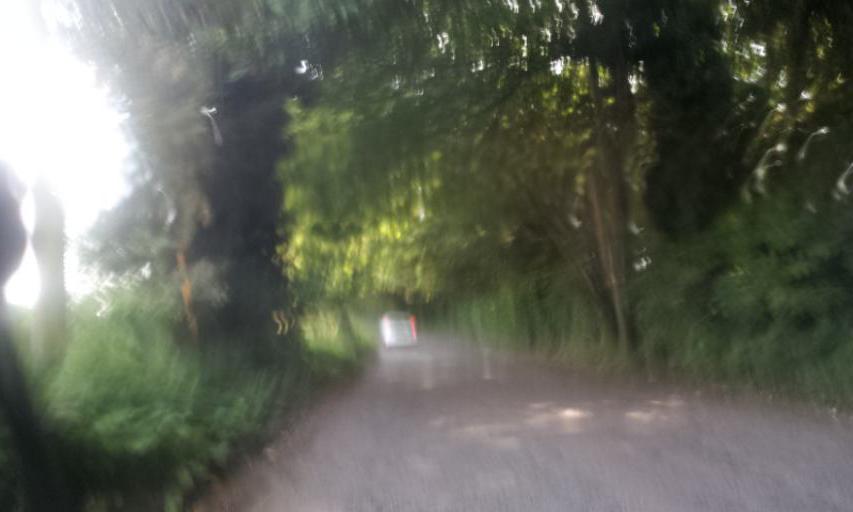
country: GB
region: England
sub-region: Kent
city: Maidstone
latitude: 51.2570
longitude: 0.5129
